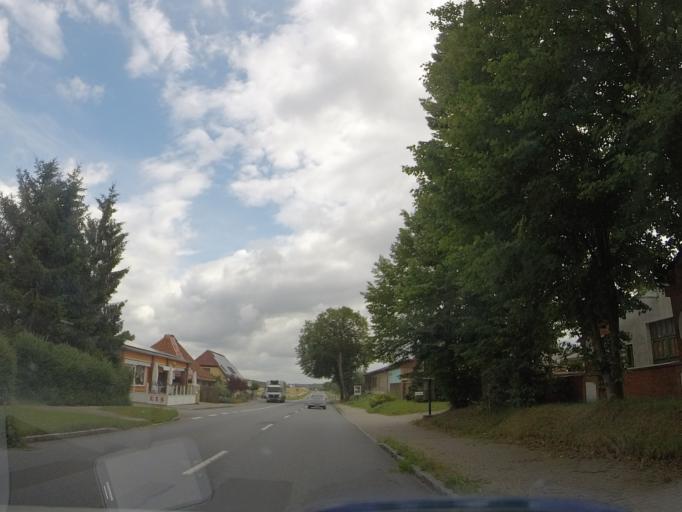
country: DE
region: Mecklenburg-Vorpommern
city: Lalendorf
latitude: 53.7646
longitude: 12.3505
